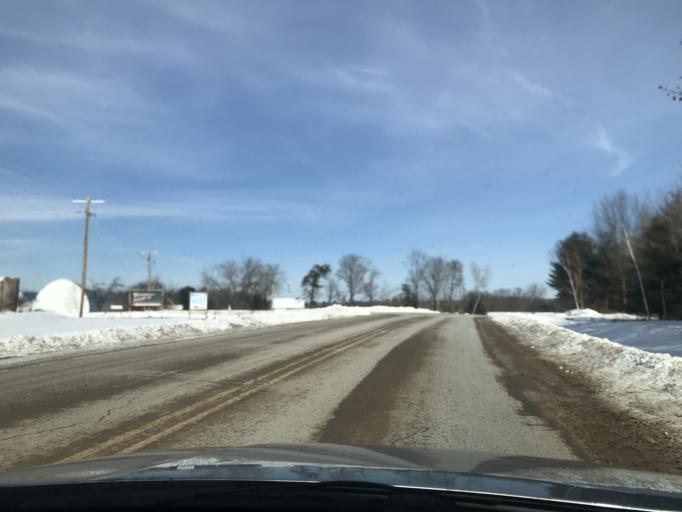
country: US
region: Wisconsin
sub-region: Oconto County
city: Oconto Falls
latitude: 45.1468
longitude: -88.1769
